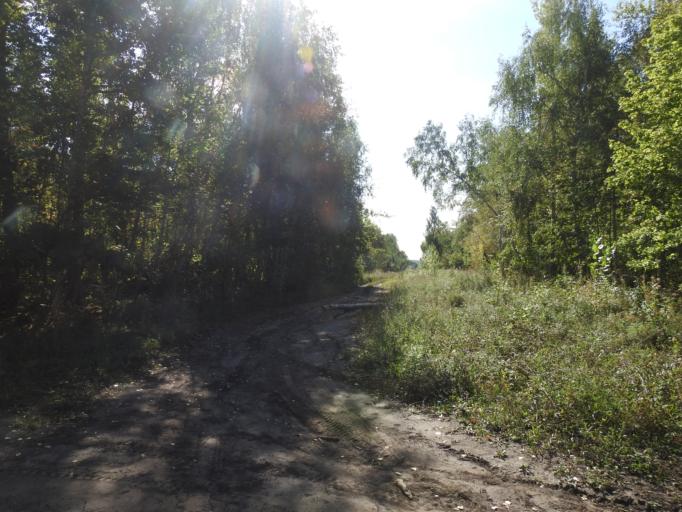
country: RU
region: Saratov
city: Novyye Burasy
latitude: 52.1494
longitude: 46.1255
